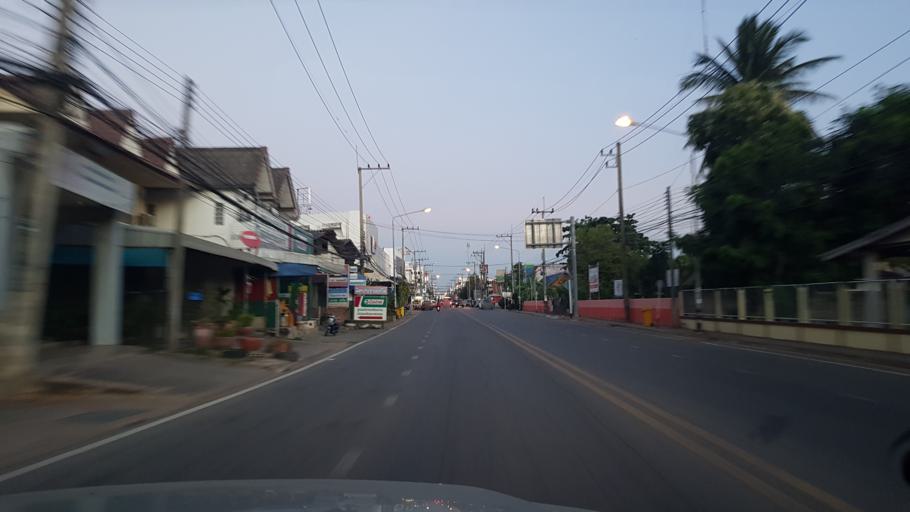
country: TH
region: Chaiyaphum
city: Phu Khiao
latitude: 16.3668
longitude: 102.1321
